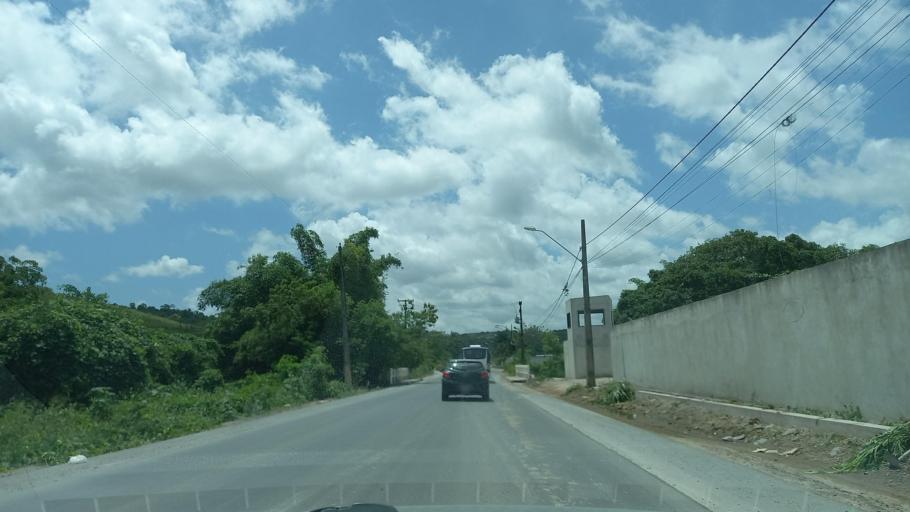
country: BR
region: Pernambuco
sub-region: Jaboatao Dos Guararapes
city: Jaboatao dos Guararapes
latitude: -8.1217
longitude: -35.0059
